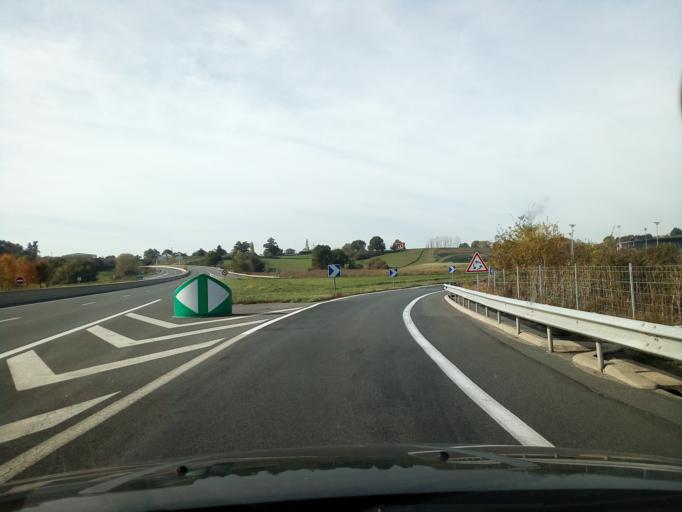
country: FR
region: Auvergne
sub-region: Departement de l'Allier
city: Saint-Victor
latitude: 46.3766
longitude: 2.5863
